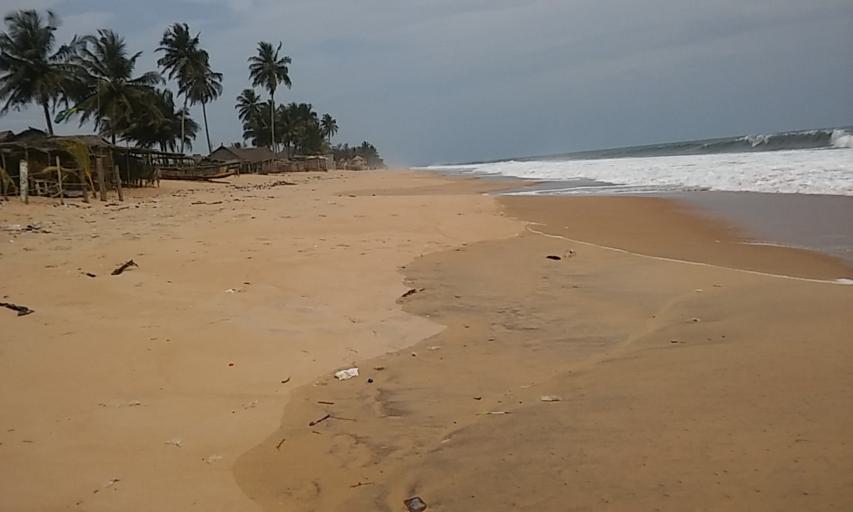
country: CI
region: Sud-Comoe
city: Grand-Bassam
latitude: 5.1972
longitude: -3.7530
